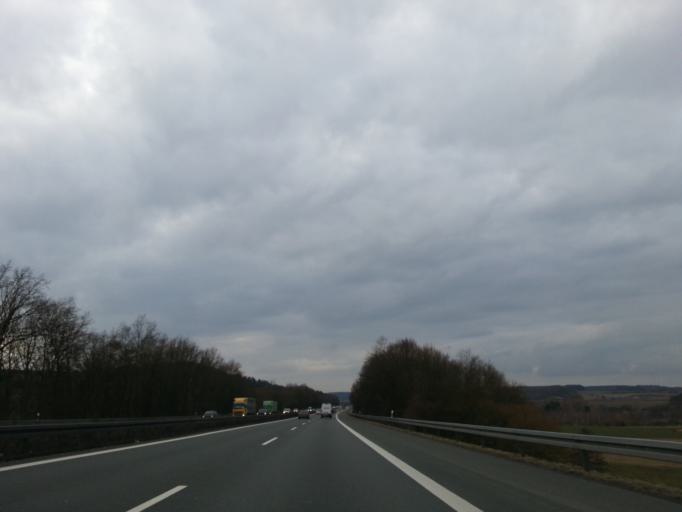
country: DE
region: Bavaria
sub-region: Regierungsbezirk Unterfranken
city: Geiselwind
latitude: 49.7647
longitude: 10.5157
